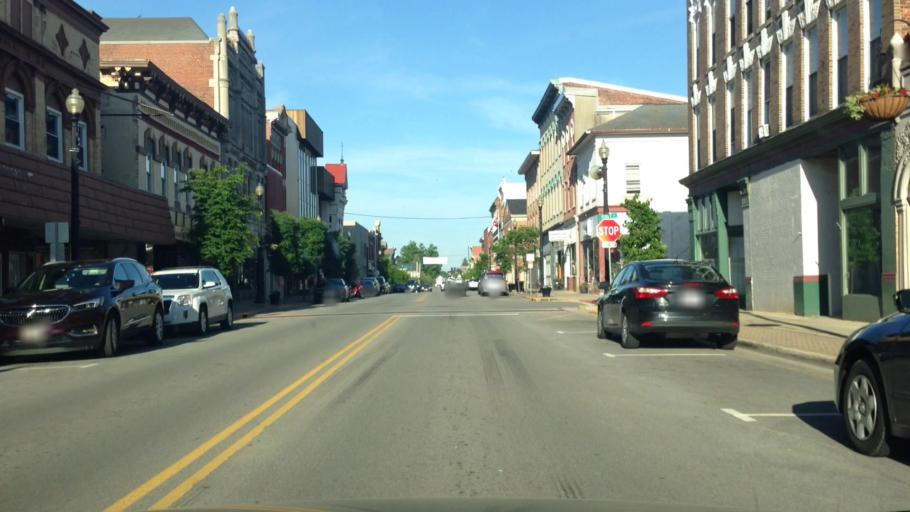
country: US
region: Ohio
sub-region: Auglaize County
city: Wapakoneta
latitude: 40.5706
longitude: -84.1951
